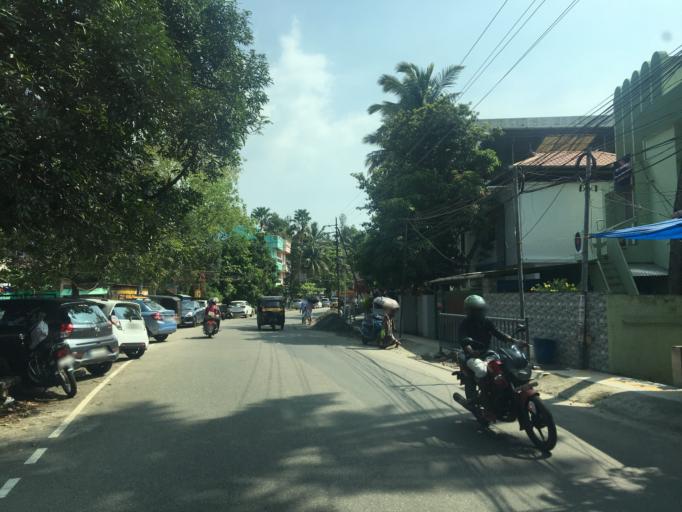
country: IN
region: Kerala
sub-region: Ernakulam
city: Cochin
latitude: 9.9648
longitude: 76.3002
